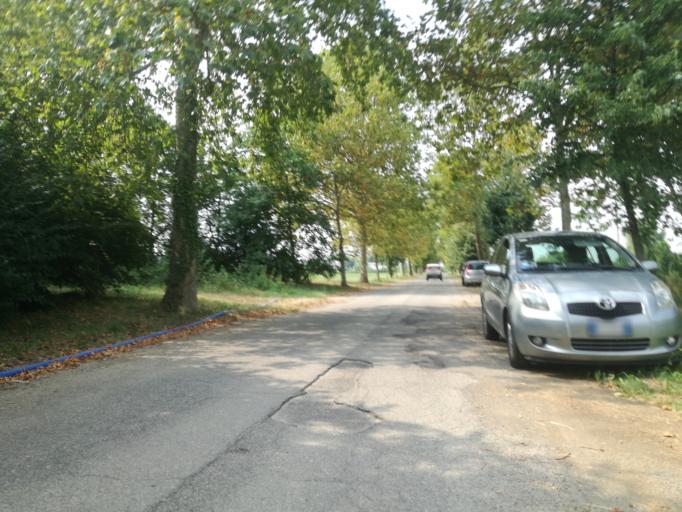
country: IT
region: Lombardy
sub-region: Provincia di Lecco
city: Verderio Superiore
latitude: 45.6637
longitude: 9.4552
